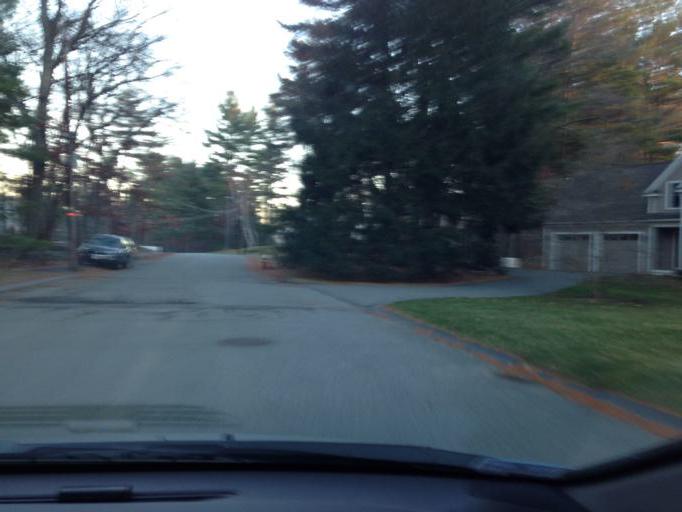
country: US
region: Massachusetts
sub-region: Middlesex County
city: Bedford
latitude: 42.4969
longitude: -71.2679
